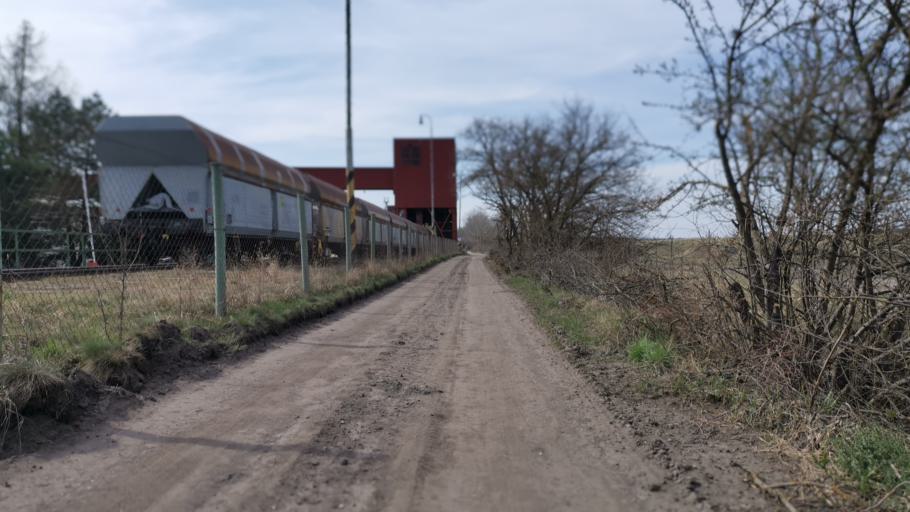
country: SK
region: Trnavsky
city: Gbely
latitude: 48.6601
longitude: 17.0756
